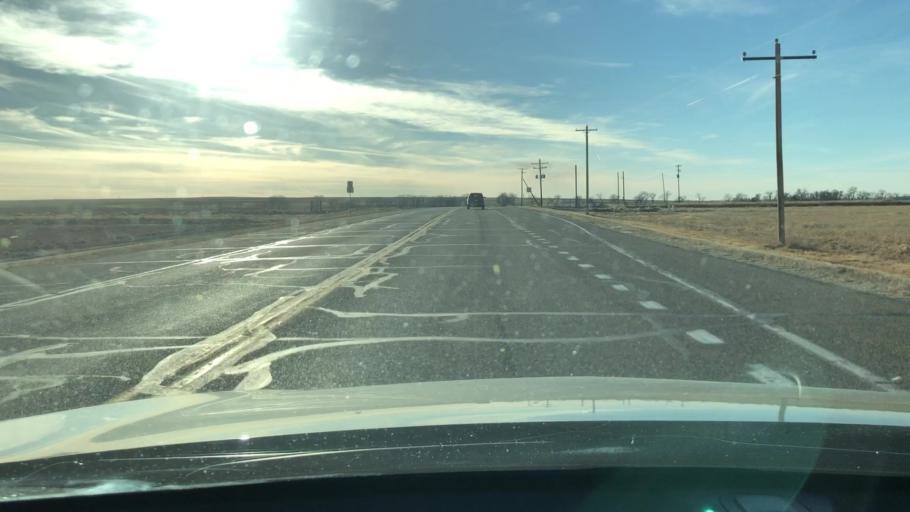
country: US
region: Colorado
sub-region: Prowers County
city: Lamar
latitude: 38.0638
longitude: -102.3447
